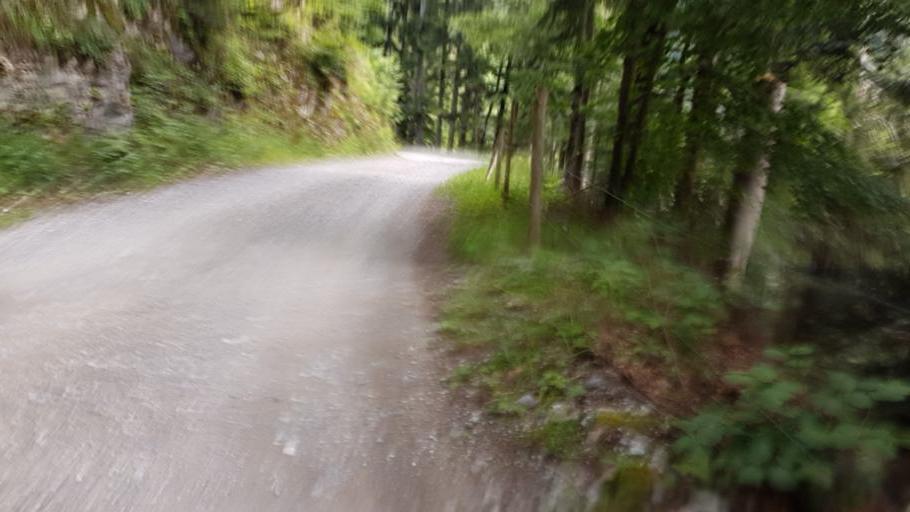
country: CH
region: Bern
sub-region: Obersimmental-Saanen District
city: Boltigen
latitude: 46.6700
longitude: 7.4616
